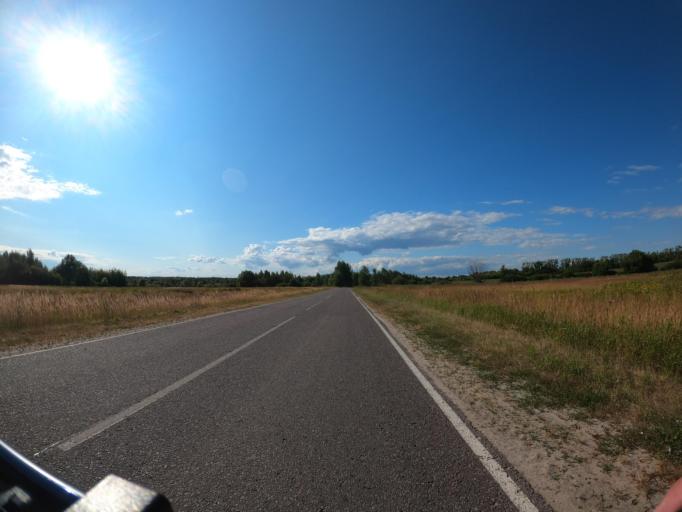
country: RU
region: Moskovskaya
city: Konobeyevo
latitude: 55.4002
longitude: 38.7112
